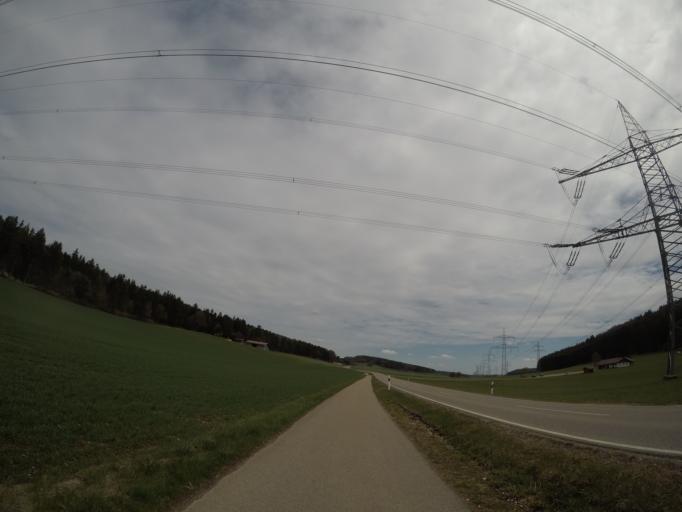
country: DE
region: Baden-Wuerttemberg
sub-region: Tuebingen Region
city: Laichingen
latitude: 48.4829
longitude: 9.6573
